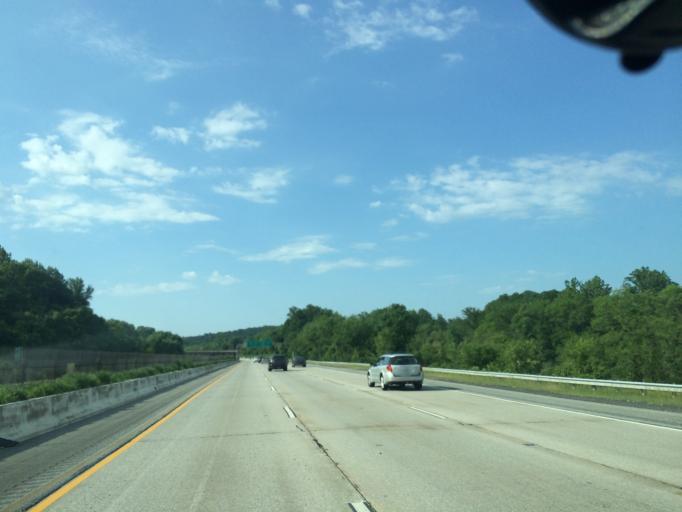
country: US
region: Maryland
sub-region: Baltimore County
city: Garrison
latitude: 39.3969
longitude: -76.7635
